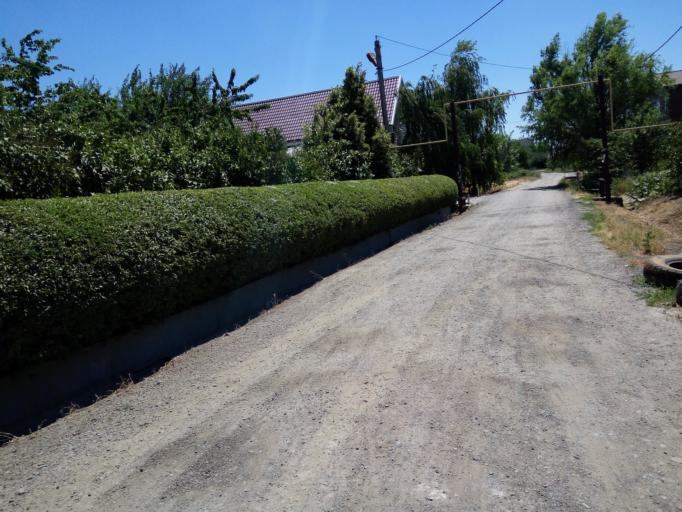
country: RU
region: Rostov
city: Bataysk
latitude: 47.1472
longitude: 39.7705
